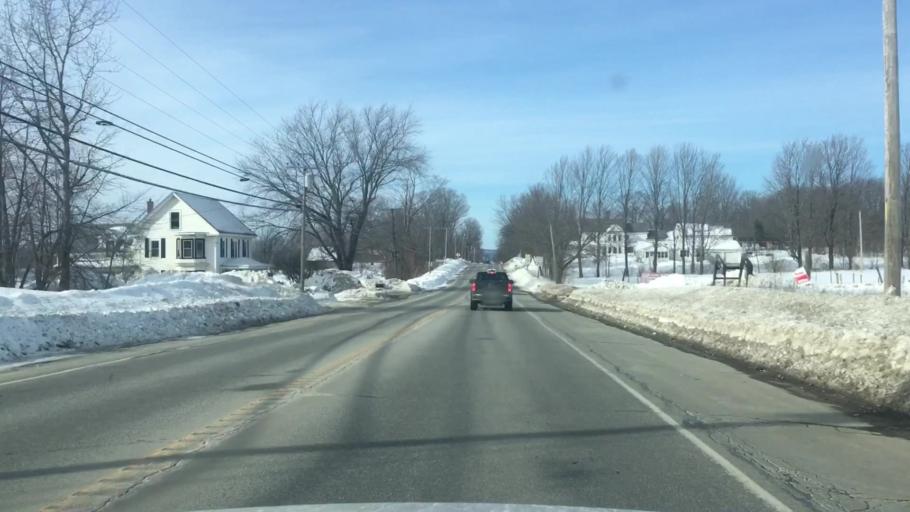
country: US
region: Maine
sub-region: Penobscot County
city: Charleston
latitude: 44.9939
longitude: -69.0190
